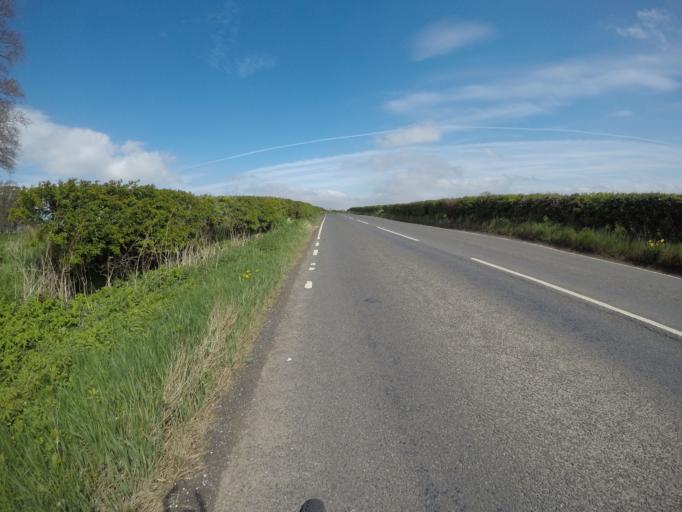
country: GB
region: Scotland
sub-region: East Ayrshire
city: Kilmaurs
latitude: 55.6648
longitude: -4.5426
